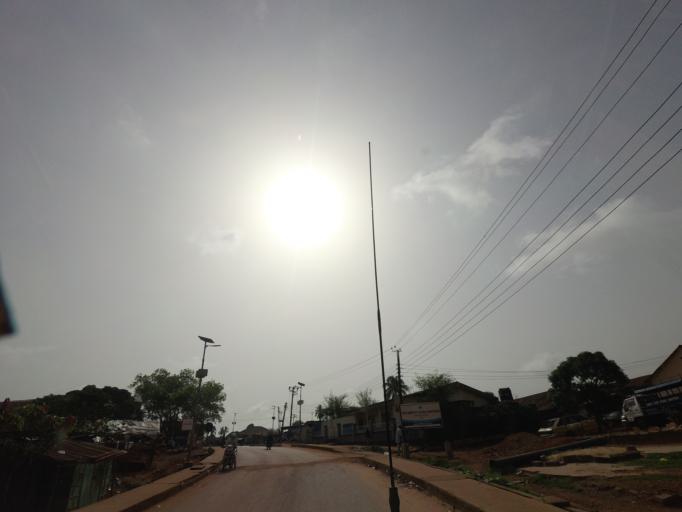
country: SL
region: Southern Province
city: Bo
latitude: 7.9579
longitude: -11.7335
